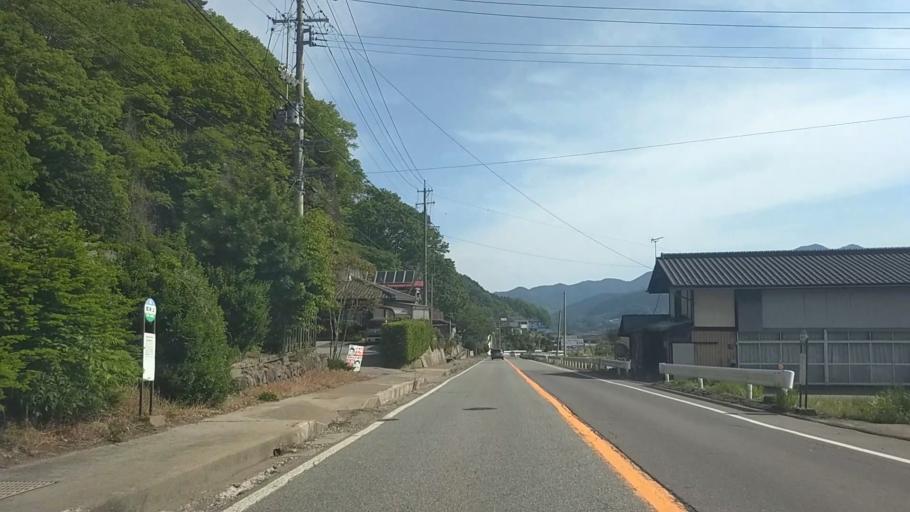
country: JP
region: Nagano
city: Saku
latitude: 36.0725
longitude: 138.4764
